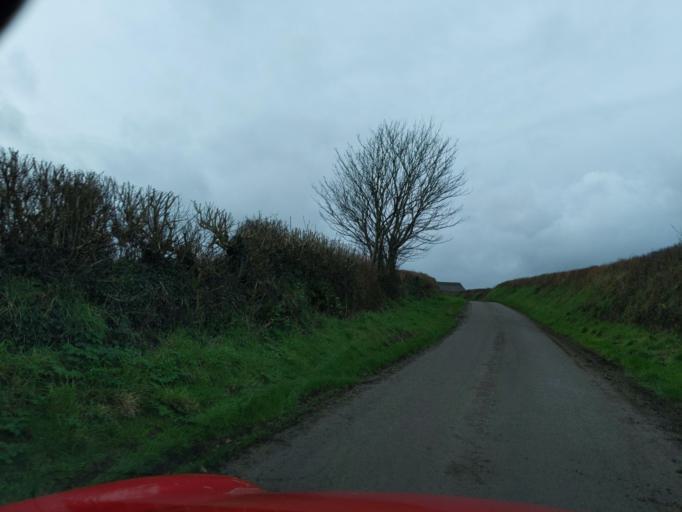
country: GB
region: England
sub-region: Cornwall
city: Duloe
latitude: 50.3481
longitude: -4.5389
